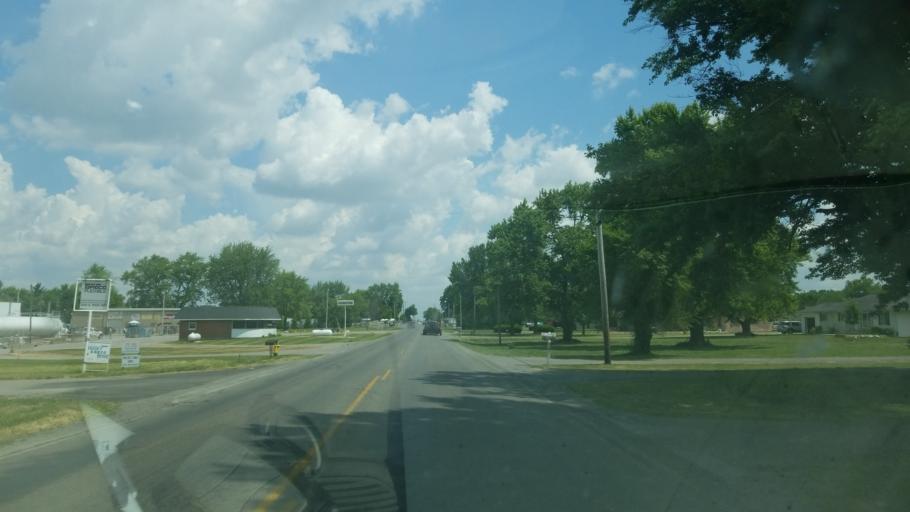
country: US
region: Ohio
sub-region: Allen County
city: Fort Shawnee
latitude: 40.6905
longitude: -84.1268
